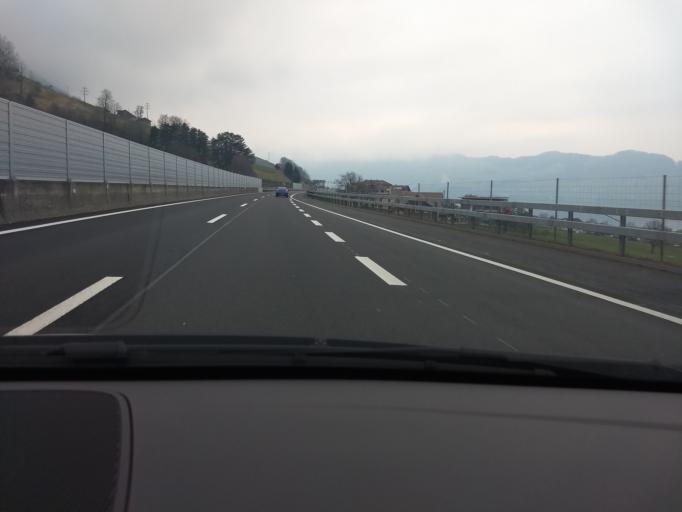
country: CH
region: Nidwalden
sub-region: Nidwalden
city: Beckenried
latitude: 46.9634
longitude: 8.4698
